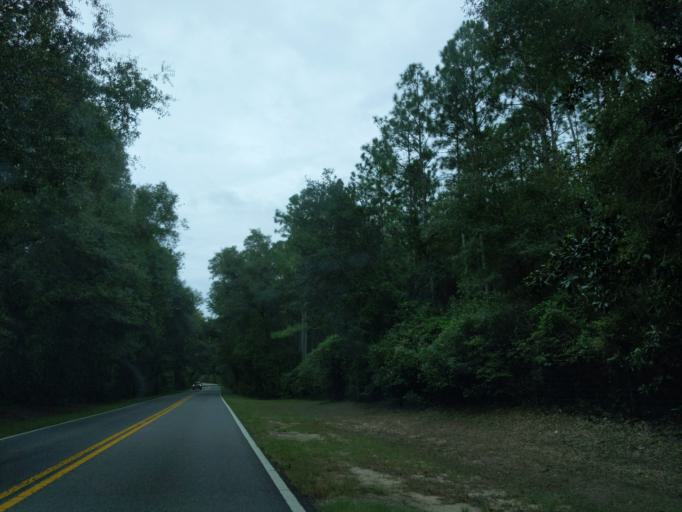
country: US
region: Florida
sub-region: Leon County
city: Woodville
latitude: 30.3672
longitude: -84.1541
